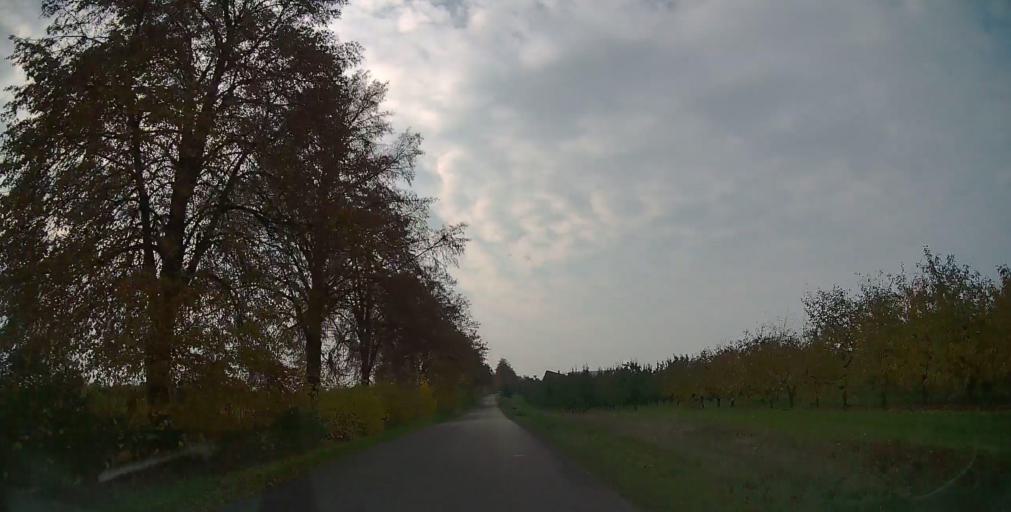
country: PL
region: Masovian Voivodeship
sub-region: Powiat grojecki
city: Mogielnica
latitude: 51.6786
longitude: 20.7141
